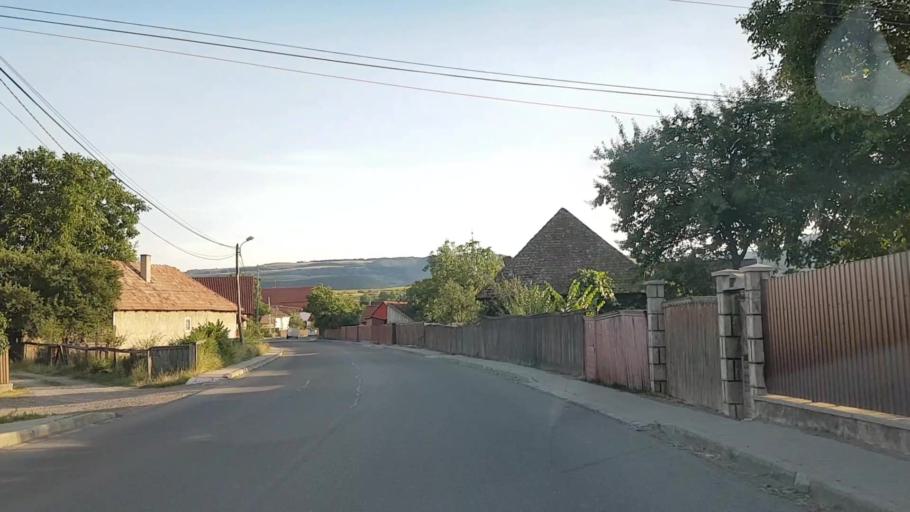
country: RO
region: Harghita
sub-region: Comuna Praid
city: Praid
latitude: 46.5560
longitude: 25.1296
